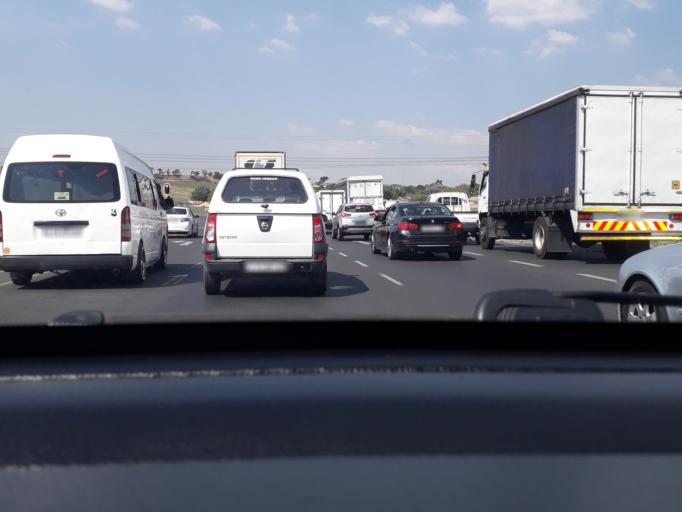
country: ZA
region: Gauteng
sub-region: City of Johannesburg Metropolitan Municipality
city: Modderfontein
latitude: -26.1013
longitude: 28.1821
